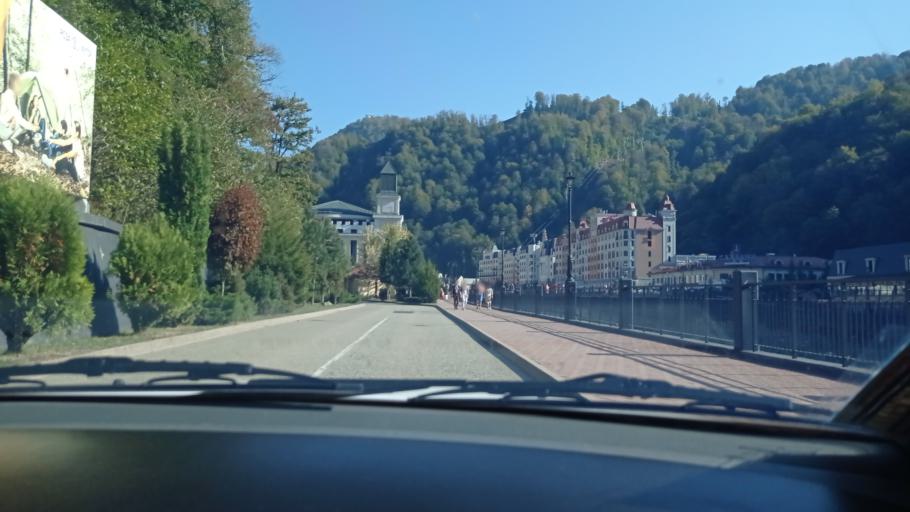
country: RU
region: Krasnodarskiy
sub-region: Sochi City
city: Krasnaya Polyana
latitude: 43.6738
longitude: 40.2908
